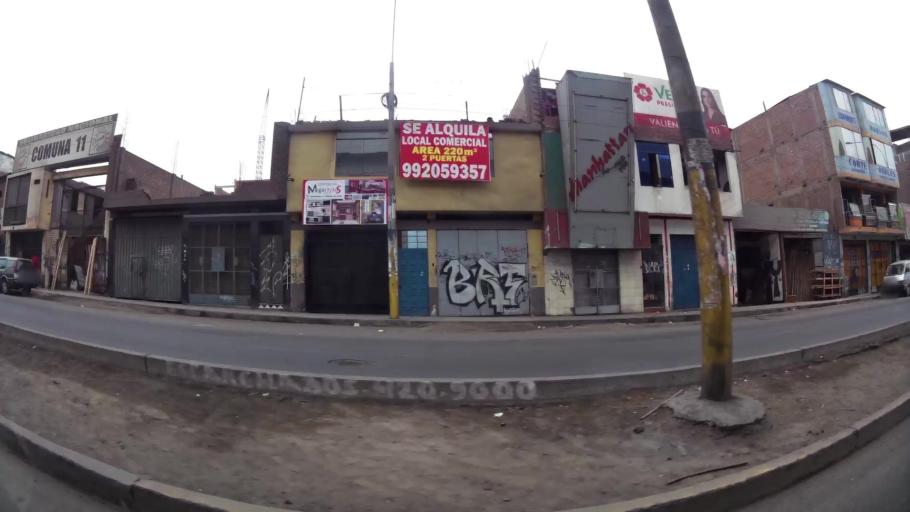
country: PE
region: Lima
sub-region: Lima
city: Independencia
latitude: -11.9665
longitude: -76.9918
